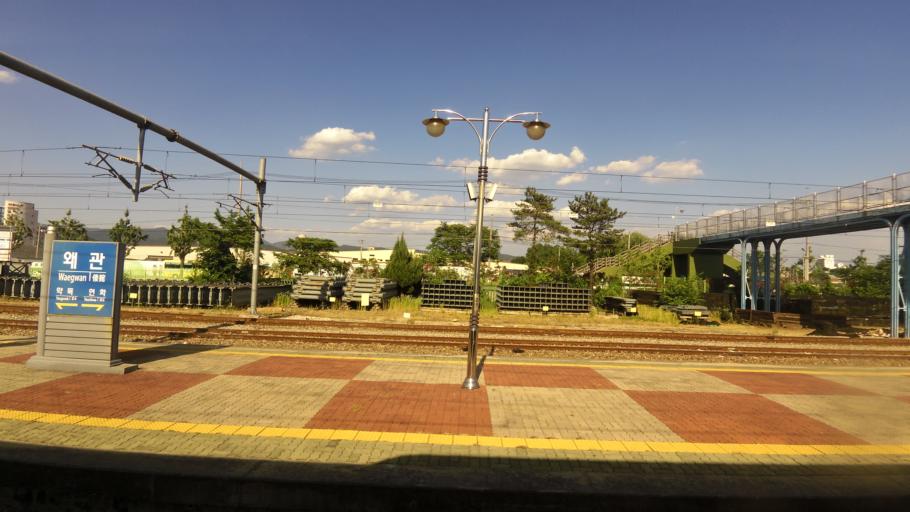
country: KR
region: Gyeongsangbuk-do
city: Waegwan
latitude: 35.9929
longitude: 128.4005
